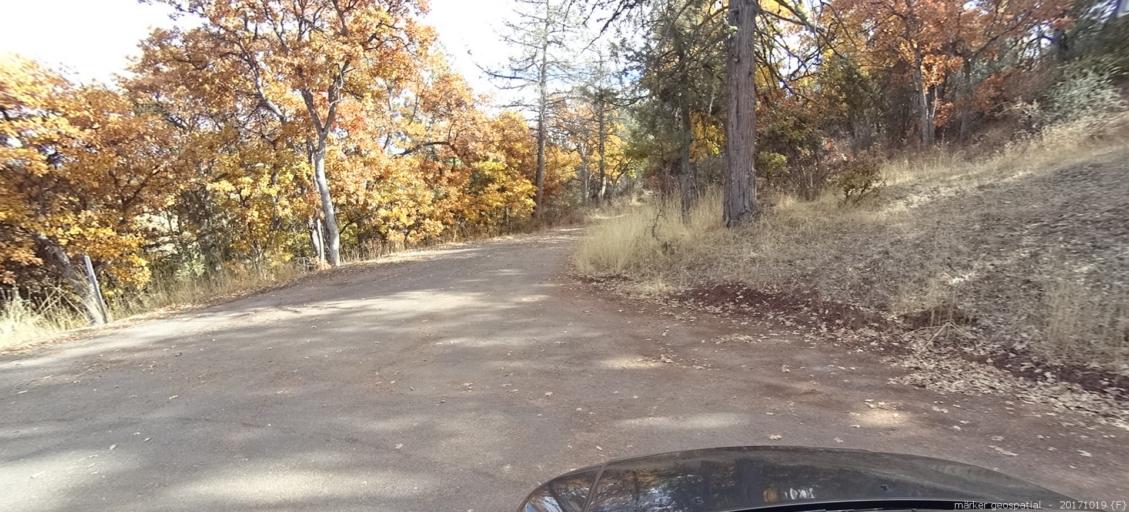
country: US
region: California
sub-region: Shasta County
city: Burney
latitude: 40.9992
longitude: -121.4384
